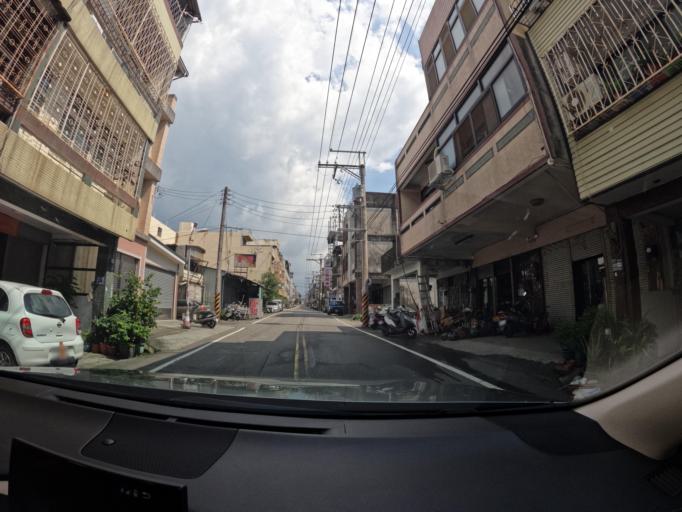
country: TW
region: Taiwan
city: Fengyuan
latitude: 24.3091
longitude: 120.8290
